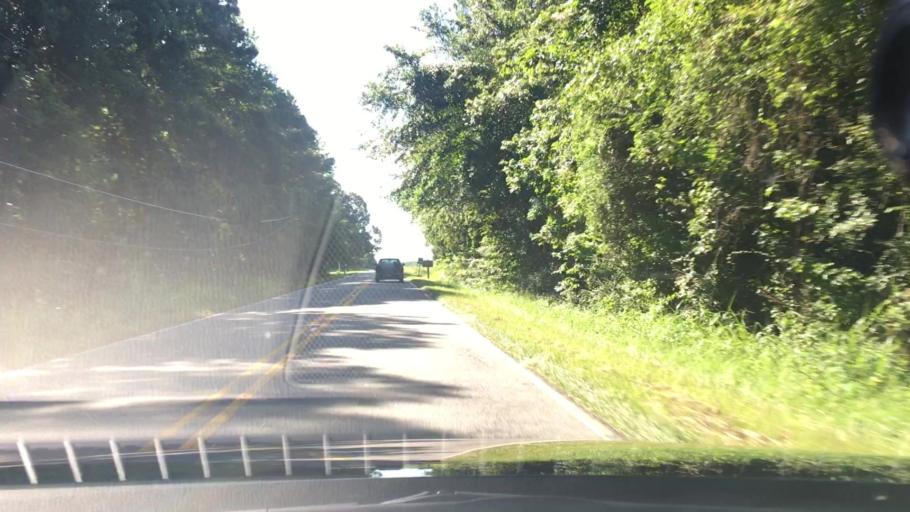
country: US
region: Georgia
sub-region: Putnam County
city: Jefferson
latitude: 33.3972
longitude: -83.2716
